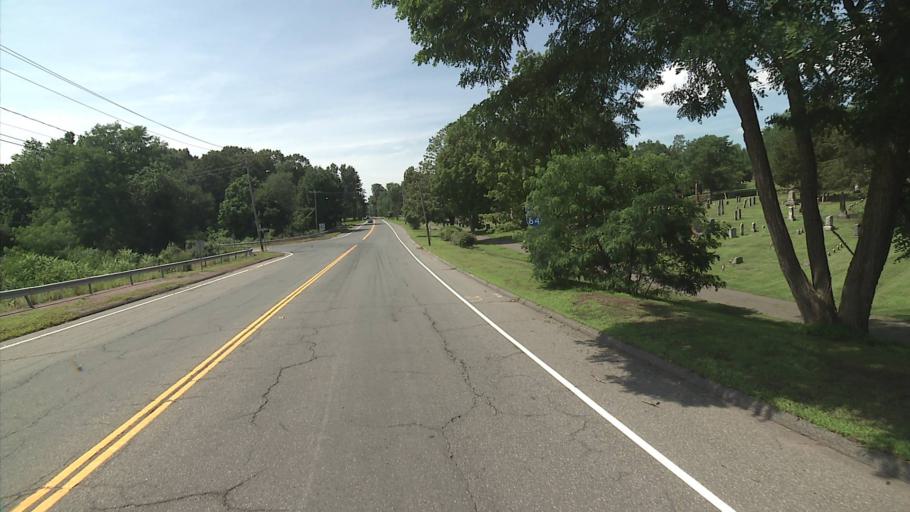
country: US
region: Connecticut
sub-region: Tolland County
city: Rockville
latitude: 41.8362
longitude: -72.4620
